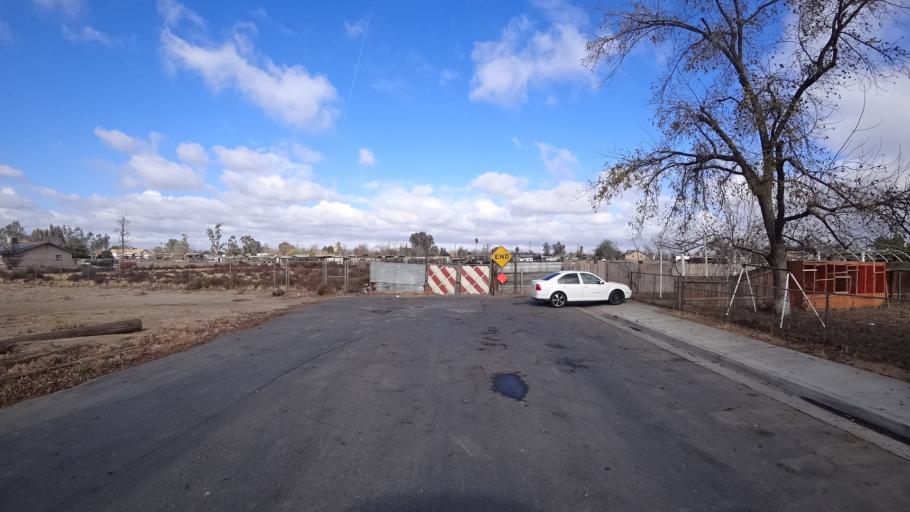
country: US
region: California
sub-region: Kern County
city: Bakersfield
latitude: 35.3266
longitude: -118.9877
